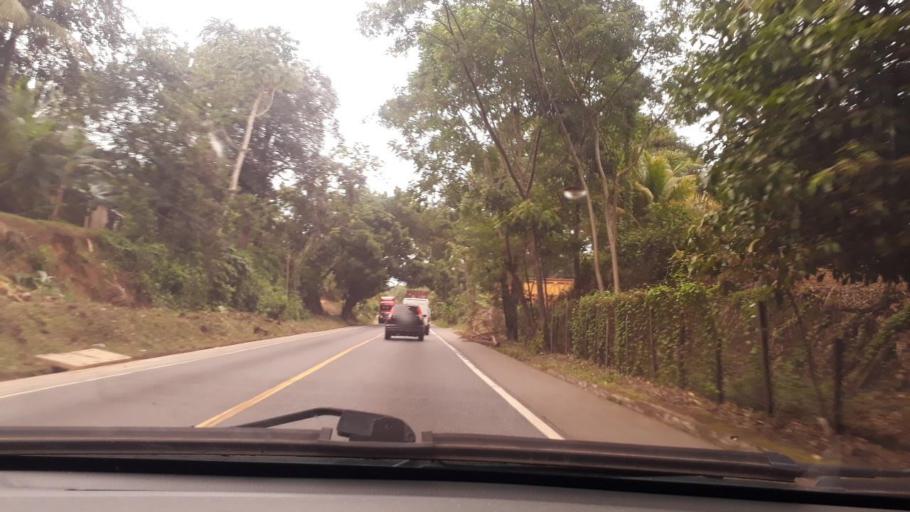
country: GT
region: Izabal
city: Morales
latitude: 15.5413
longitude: -88.7251
